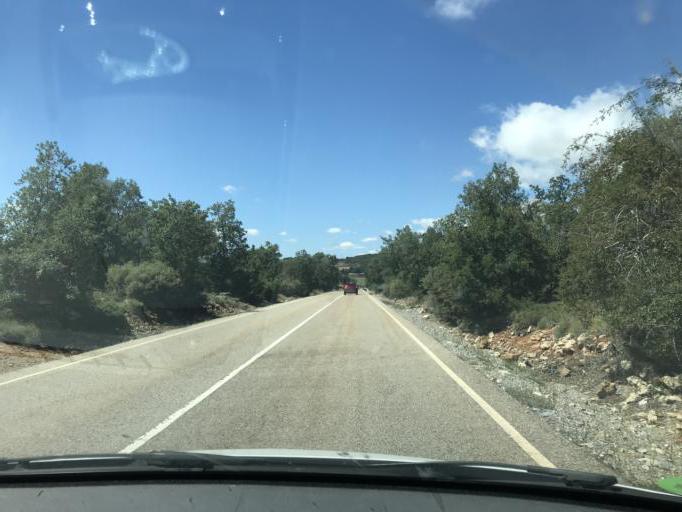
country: ES
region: Castille and Leon
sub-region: Provincia de Palencia
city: Dehesa de Montejo
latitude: 42.8262
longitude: -4.4878
